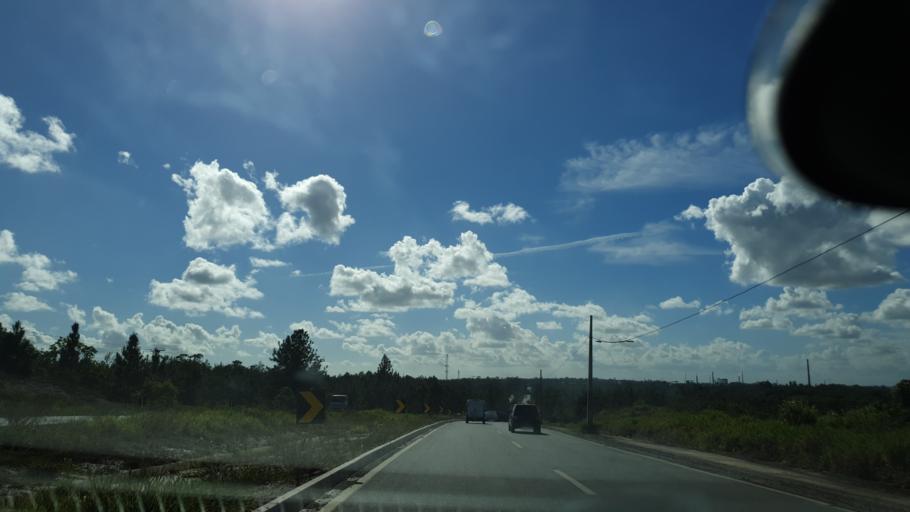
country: BR
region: Bahia
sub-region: Camacari
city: Camacari
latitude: -12.6824
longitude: -38.2906
